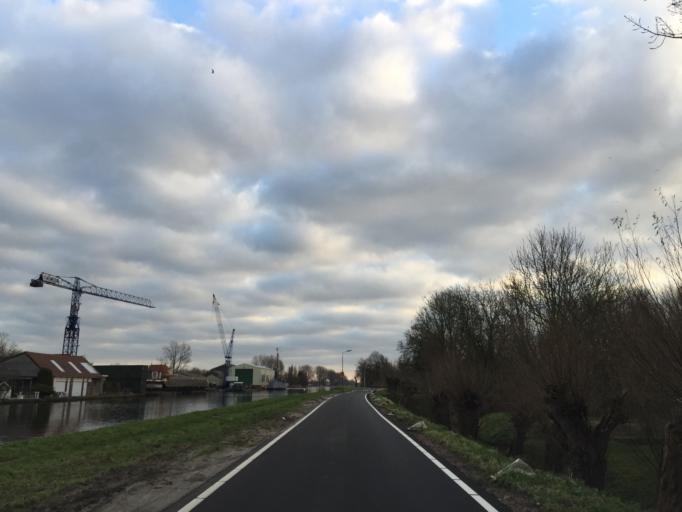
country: NL
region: South Holland
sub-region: Gemeente Delft
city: Delft
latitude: 51.9815
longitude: 4.3784
